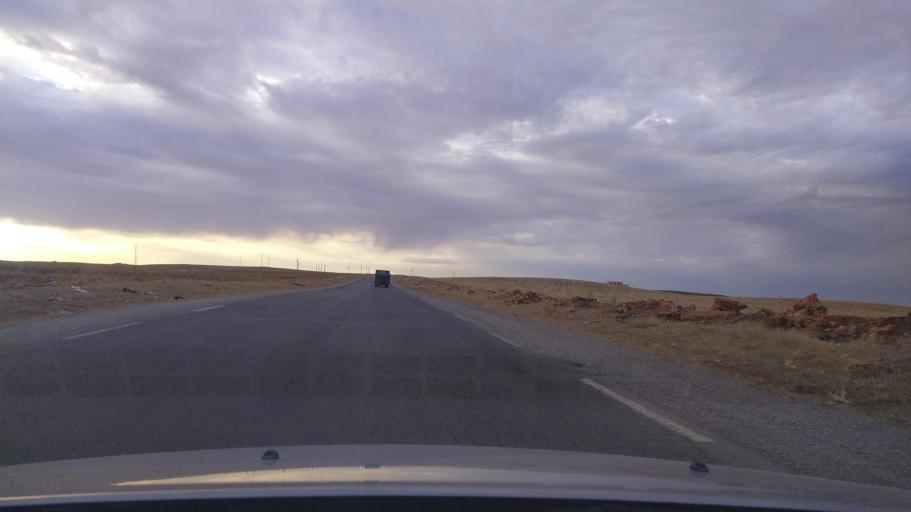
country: DZ
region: Tiaret
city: Frenda
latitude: 34.9859
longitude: 1.1388
